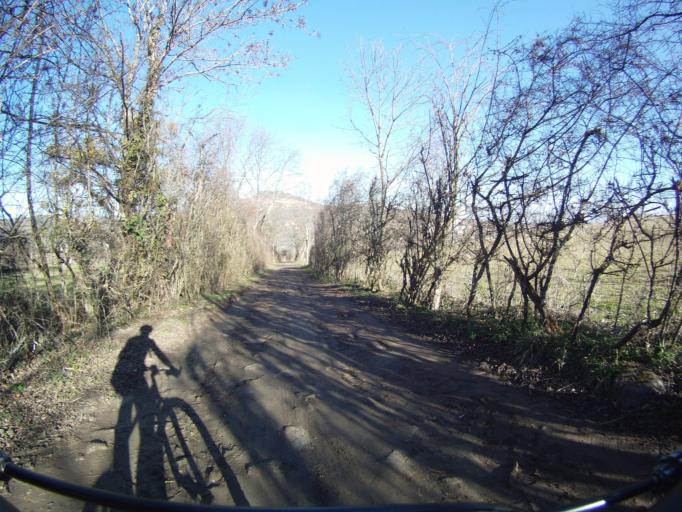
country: FR
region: Auvergne
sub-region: Departement du Puy-de-Dome
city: Romagnat
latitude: 45.7208
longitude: 3.0847
